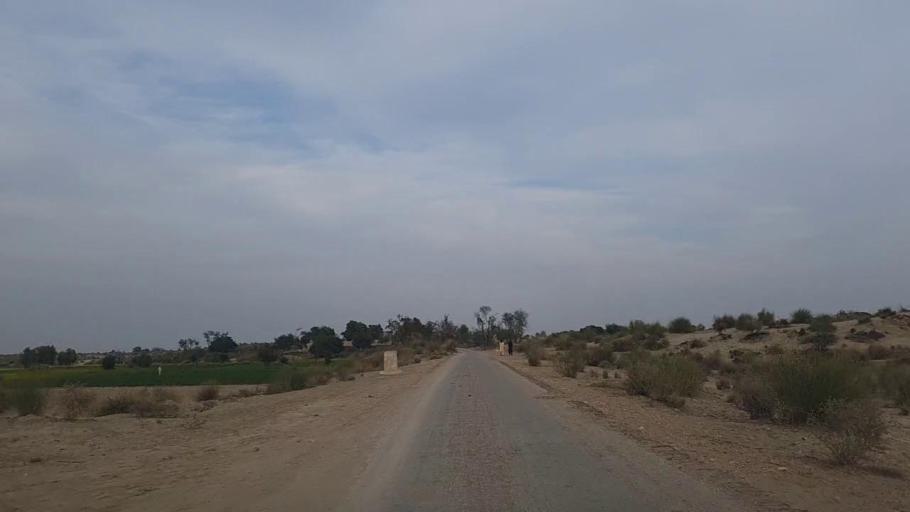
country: PK
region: Sindh
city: Daur
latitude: 26.5120
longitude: 68.4684
